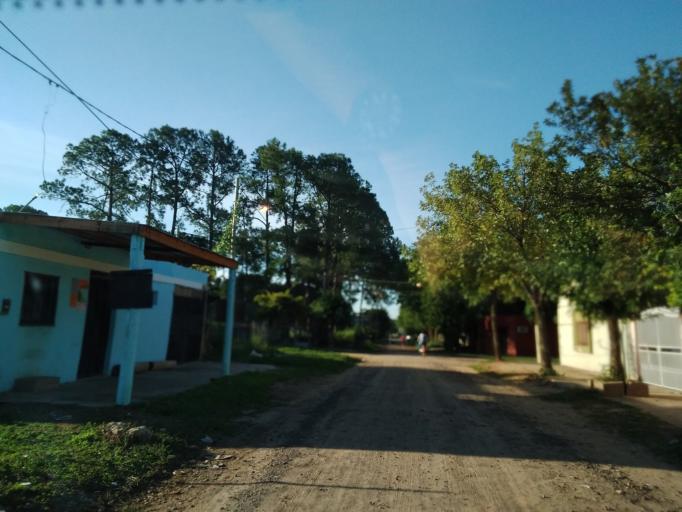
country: AR
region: Corrientes
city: Corrientes
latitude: -27.5031
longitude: -58.8060
